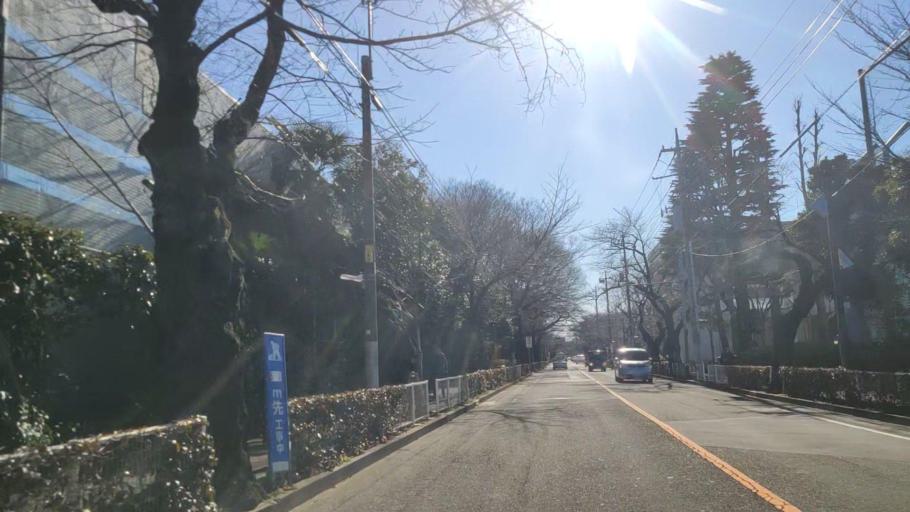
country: JP
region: Tokyo
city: Musashino
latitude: 35.7193
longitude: 139.5677
